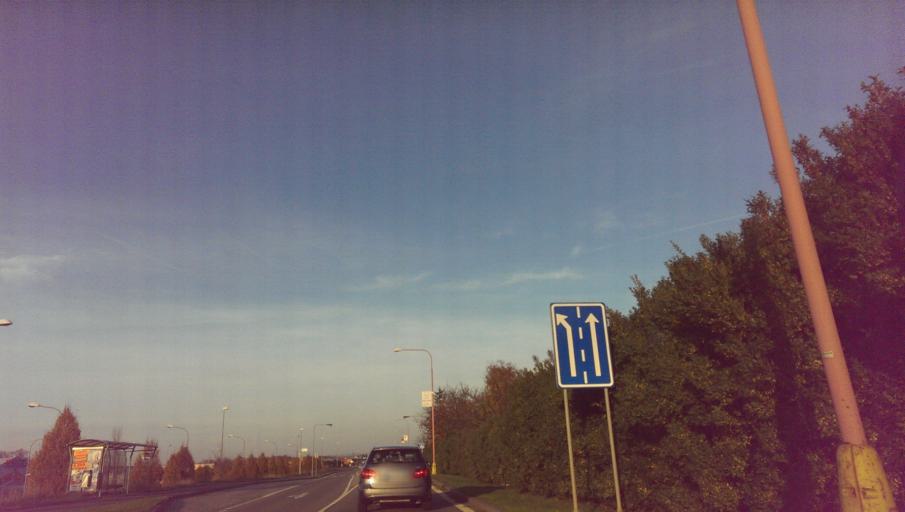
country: CZ
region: Zlin
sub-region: Okres Uherske Hradiste
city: Uherske Hradiste
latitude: 49.0770
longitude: 17.4842
